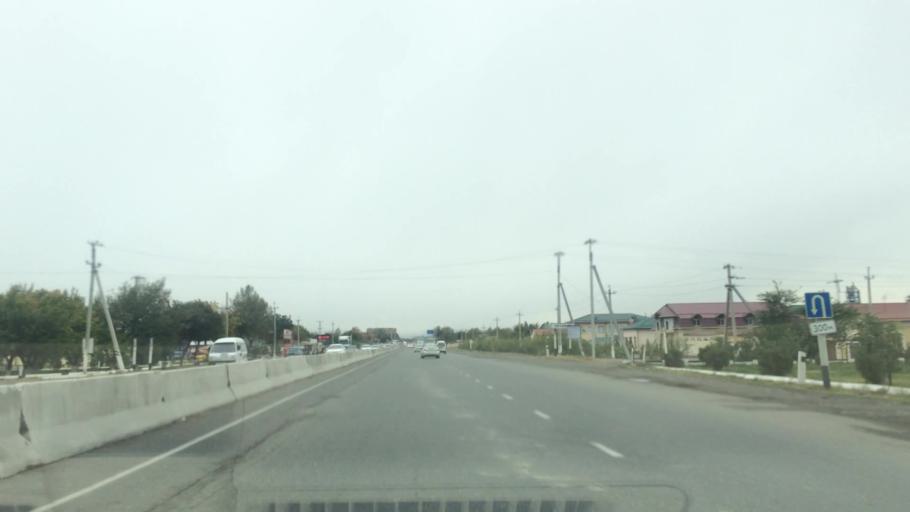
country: UZ
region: Samarqand
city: Jomboy
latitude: 39.7023
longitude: 67.0780
